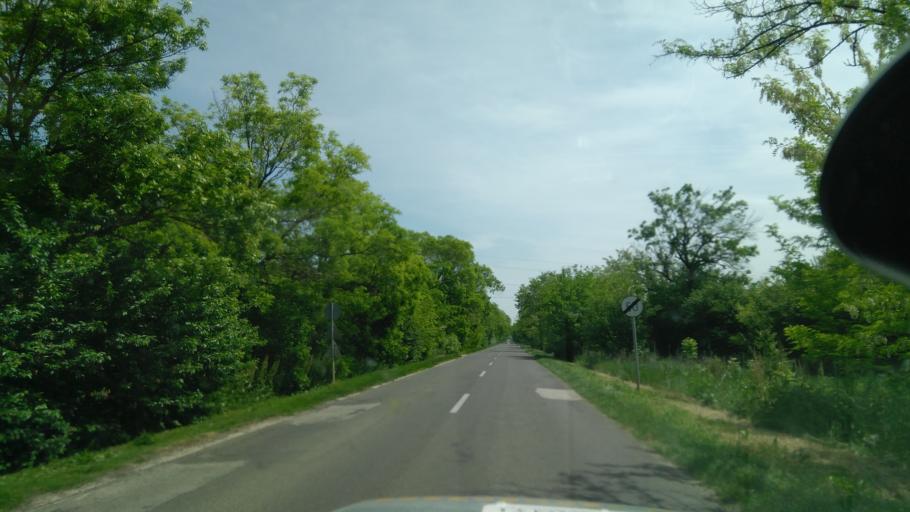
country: HU
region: Csongrad
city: Fabiansebestyen
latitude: 46.5756
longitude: 20.4442
